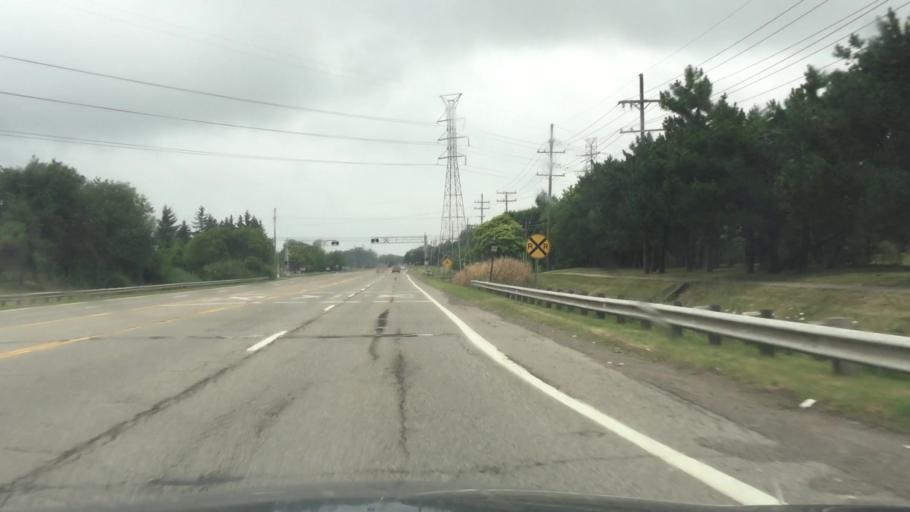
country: US
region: Michigan
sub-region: Oakland County
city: Wixom
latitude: 42.5142
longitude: -83.5370
